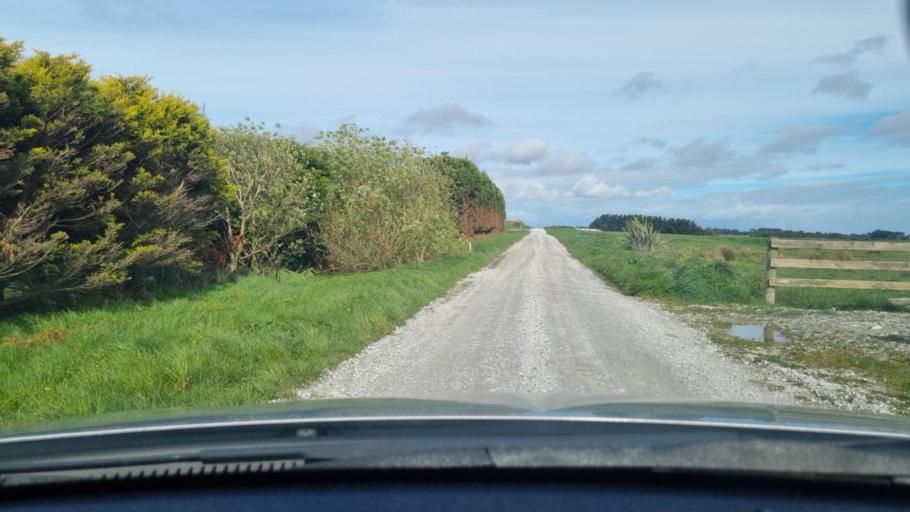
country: NZ
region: Southland
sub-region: Invercargill City
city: Invercargill
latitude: -46.4543
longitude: 168.3842
